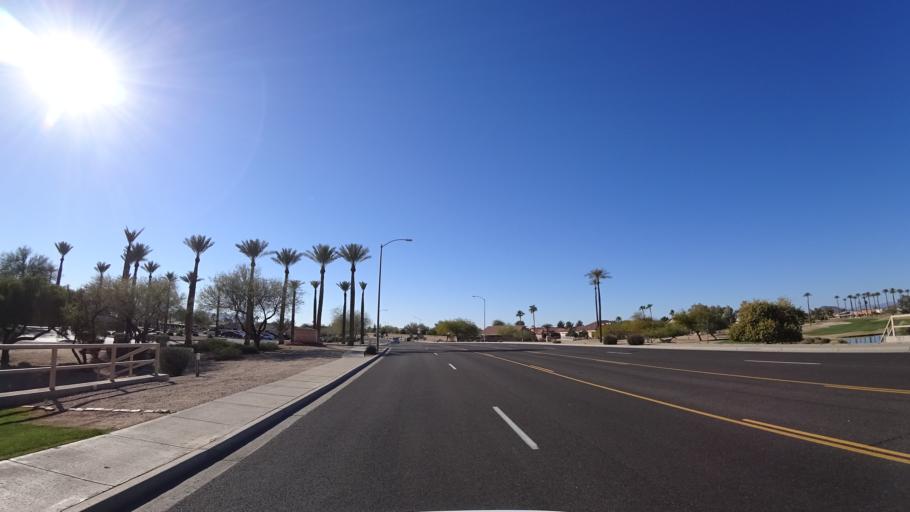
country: US
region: Arizona
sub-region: Maricopa County
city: Sun City West
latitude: 33.6875
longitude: -112.3610
